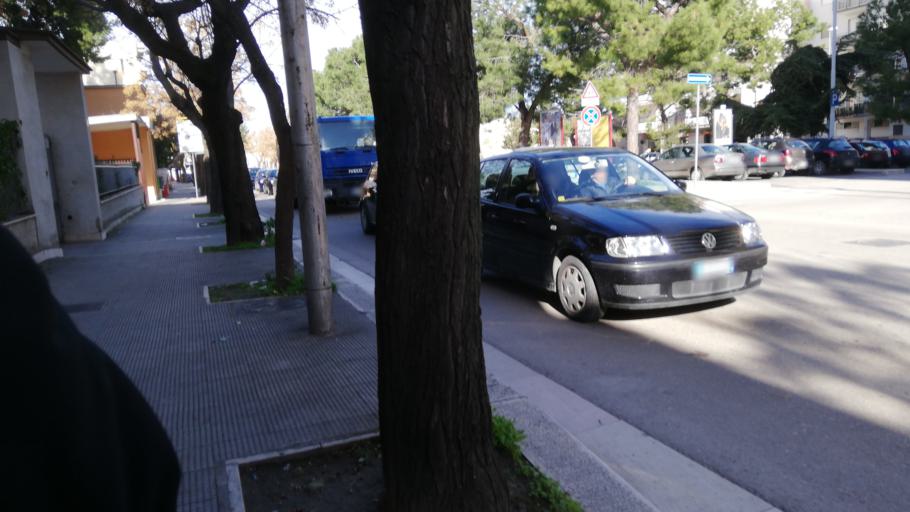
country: IT
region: Apulia
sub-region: Provincia di Barletta - Andria - Trani
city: Andria
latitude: 41.2351
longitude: 16.3087
